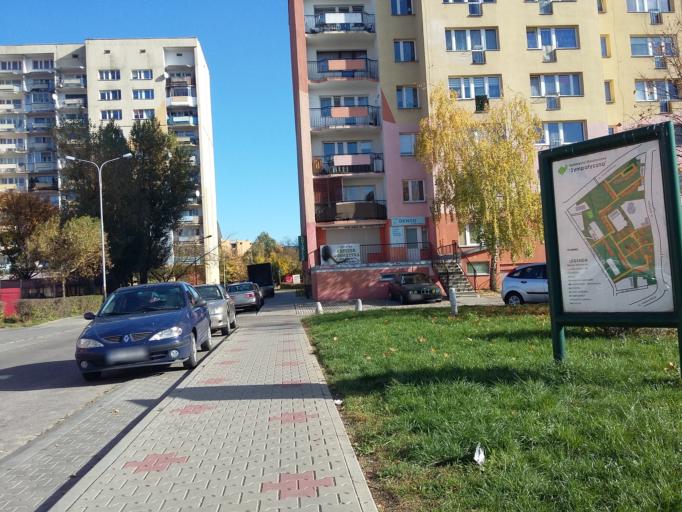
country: PL
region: Lodz Voivodeship
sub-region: Powiat pabianicki
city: Ksawerow
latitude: 51.7439
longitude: 19.4007
